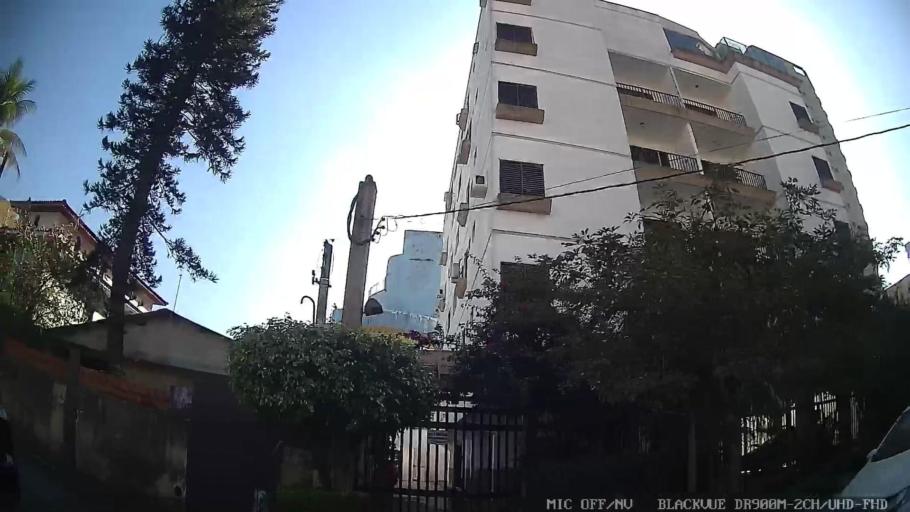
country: BR
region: Sao Paulo
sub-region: Guaruja
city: Guaruja
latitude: -24.0087
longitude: -46.2715
